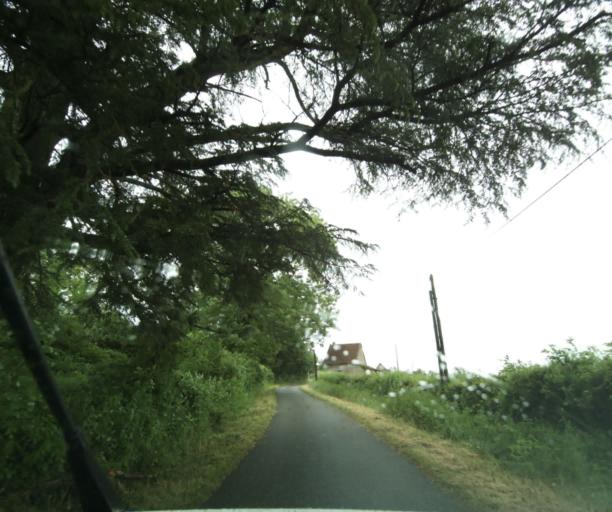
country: FR
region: Bourgogne
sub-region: Departement de Saone-et-Loire
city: Saint-Vallier
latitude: 46.4936
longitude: 4.4601
